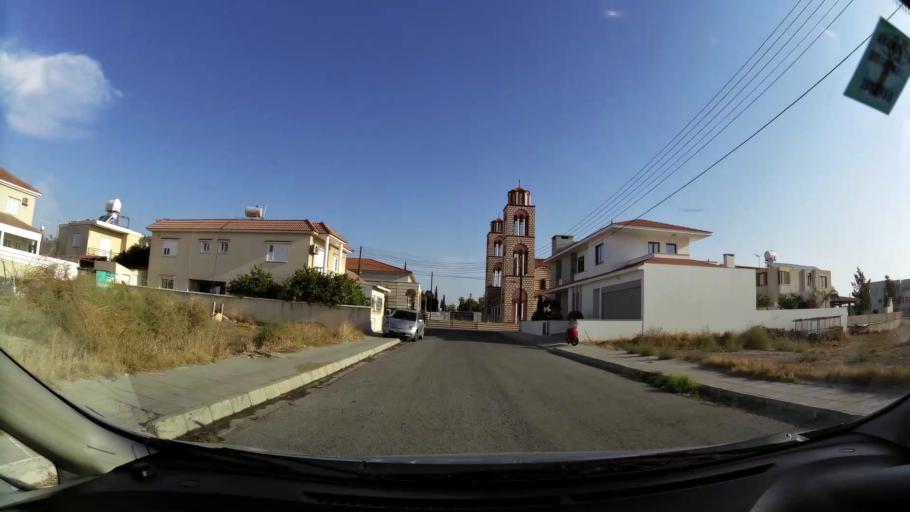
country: CY
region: Larnaka
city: Aradippou
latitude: 34.9434
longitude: 33.5939
